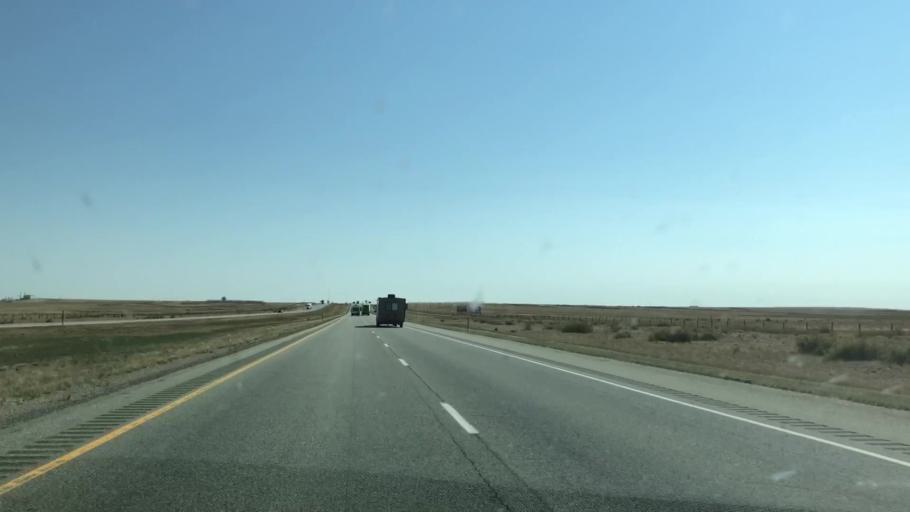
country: US
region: Wyoming
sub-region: Carbon County
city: Rawlins
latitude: 41.6682
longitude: -108.0101
